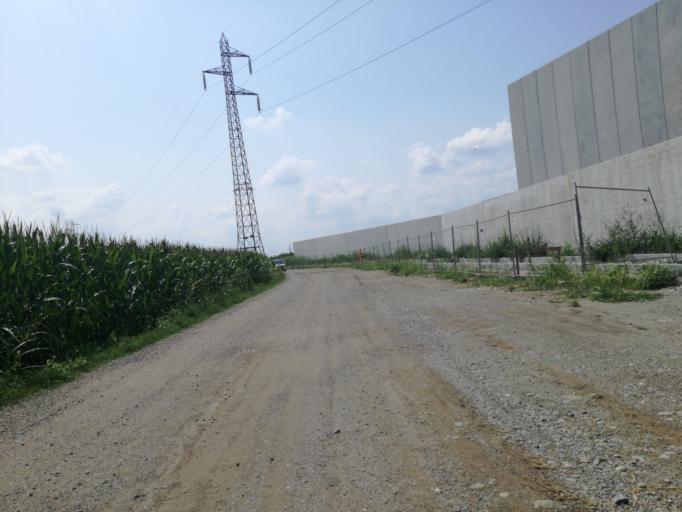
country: IT
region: Lombardy
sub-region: Provincia di Bergamo
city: Calusco d'Adda
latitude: 45.6823
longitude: 9.4738
